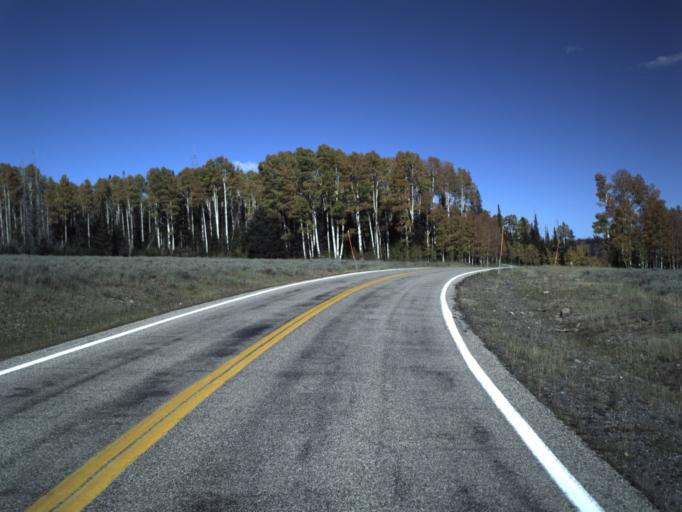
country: US
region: Utah
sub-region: Iron County
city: Parowan
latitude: 37.6581
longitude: -112.7496
